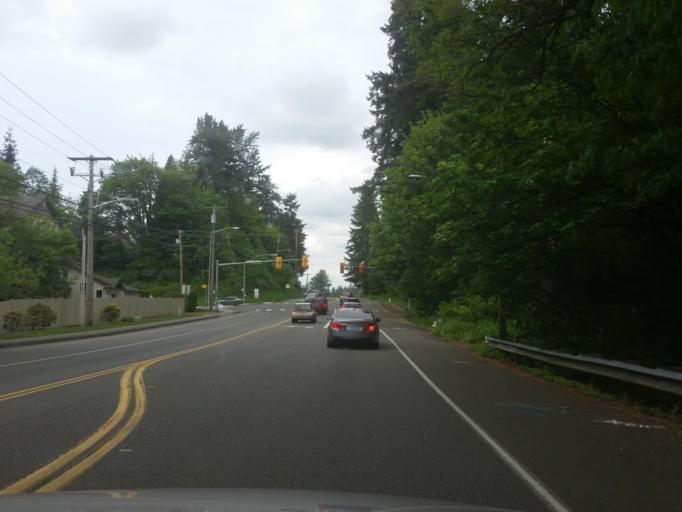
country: US
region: Washington
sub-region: King County
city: Inglewood-Finn Hill
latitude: 47.7299
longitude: -122.2078
